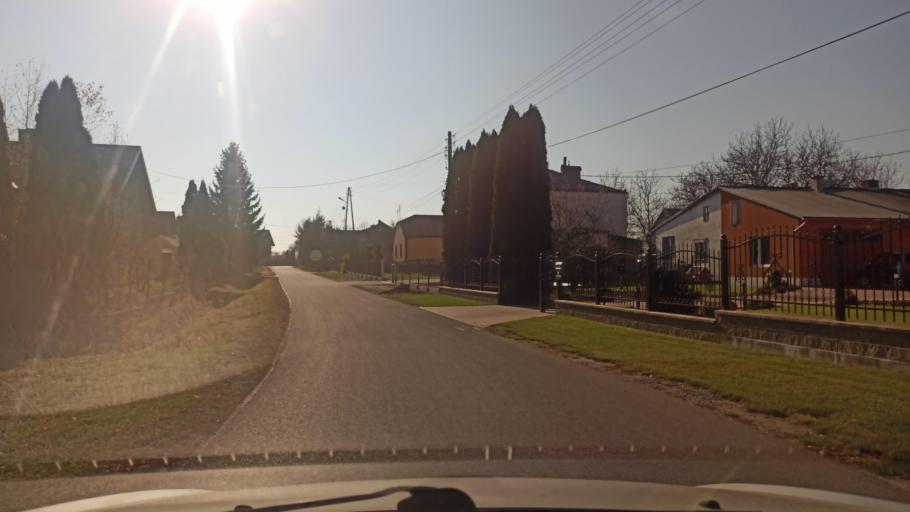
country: PL
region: Subcarpathian Voivodeship
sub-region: Powiat jaroslawski
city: Radymno
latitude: 49.9427
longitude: 22.8155
